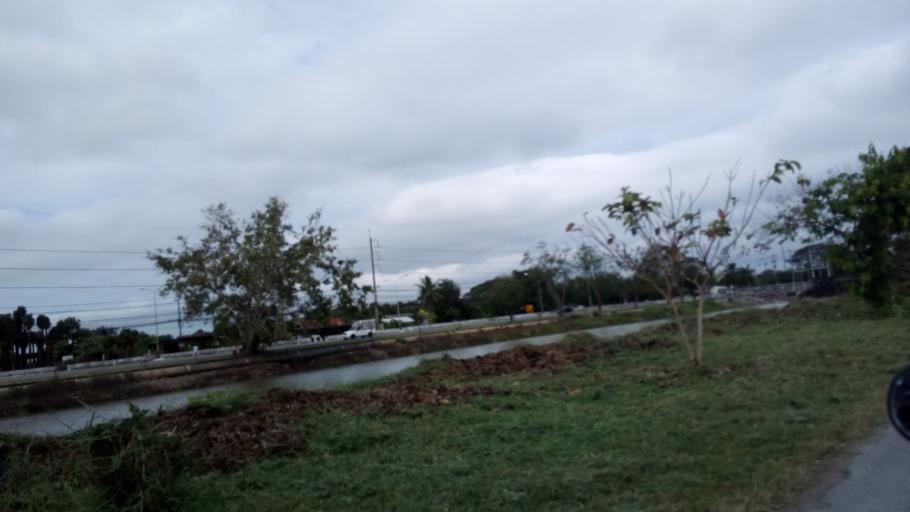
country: TH
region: Pathum Thani
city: Nong Suea
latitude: 14.0699
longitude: 100.8754
